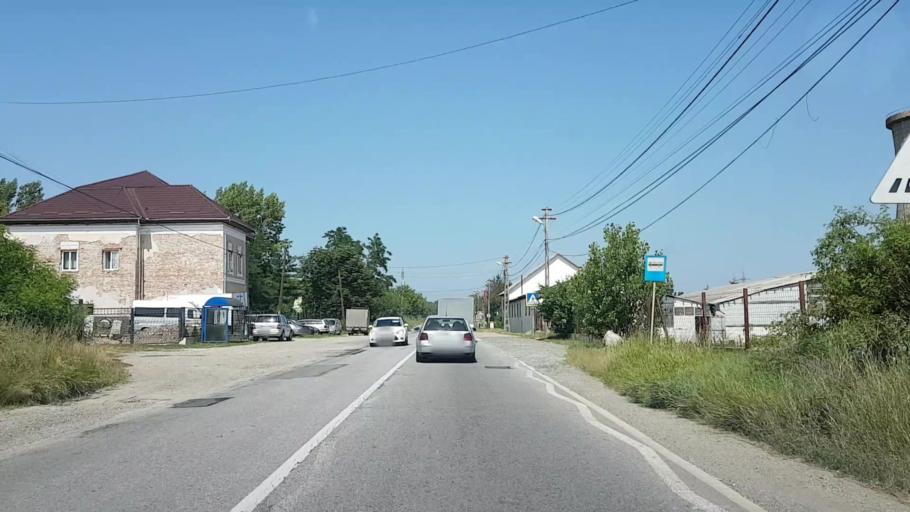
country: RO
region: Cluj
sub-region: Comuna Cusdrioara
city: Cusdrioara
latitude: 47.1630
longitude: 23.8956
